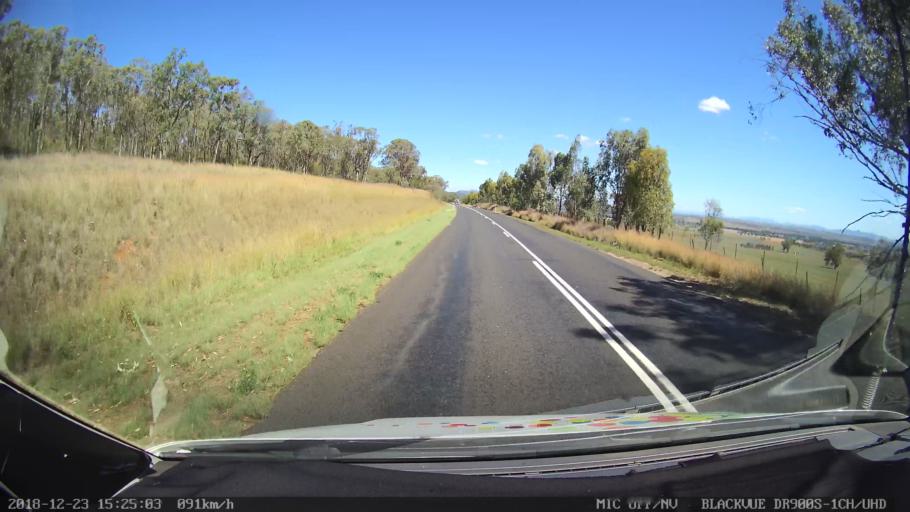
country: AU
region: New South Wales
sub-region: Tamworth Municipality
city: Manilla
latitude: -30.8996
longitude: 150.8270
